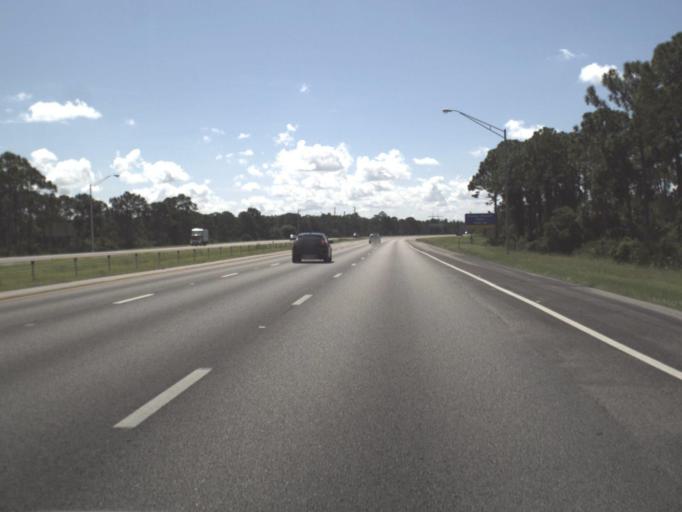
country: US
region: Florida
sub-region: Charlotte County
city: Charlotte Park
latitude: 26.8730
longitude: -81.9787
